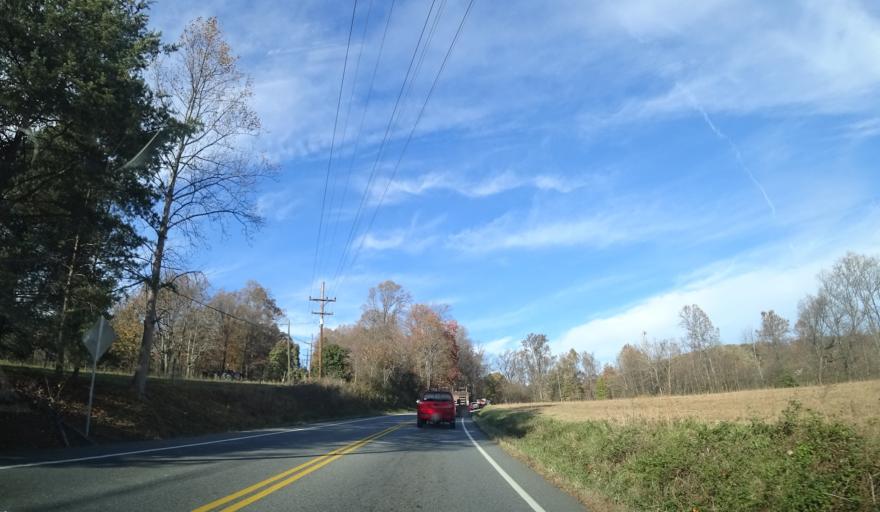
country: US
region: Virginia
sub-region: Greene County
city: Stanardsville
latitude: 38.3176
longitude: -78.4765
